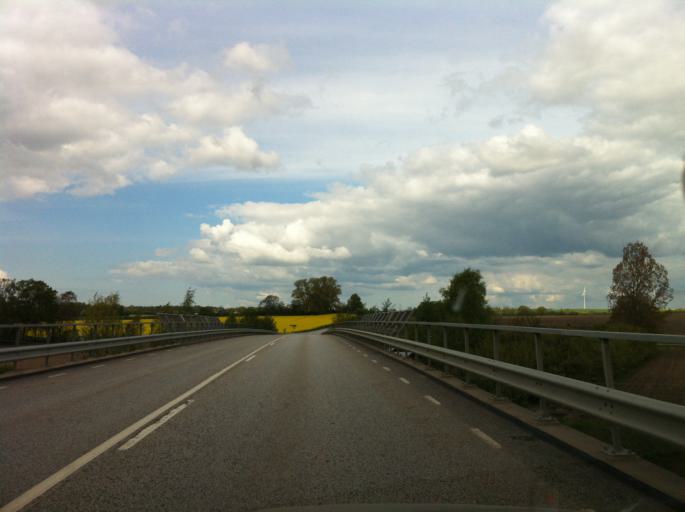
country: SE
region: Skane
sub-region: Kavlinge Kommun
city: Loddekopinge
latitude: 55.8219
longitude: 13.0368
